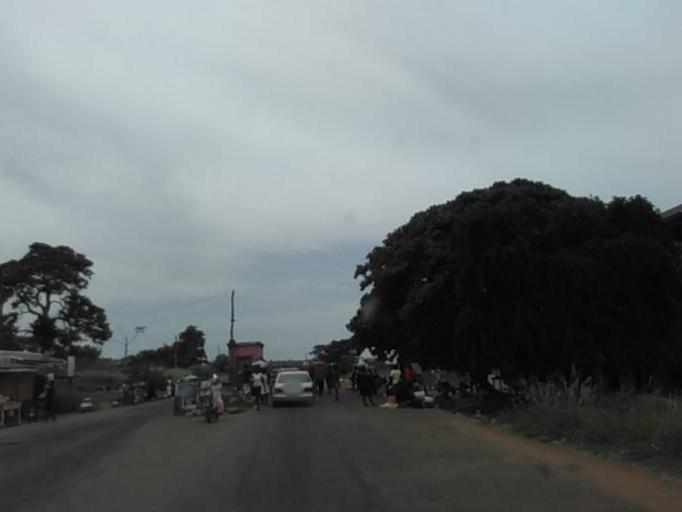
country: GH
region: Ashanti
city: Mampong
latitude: 7.0937
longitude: -1.4061
